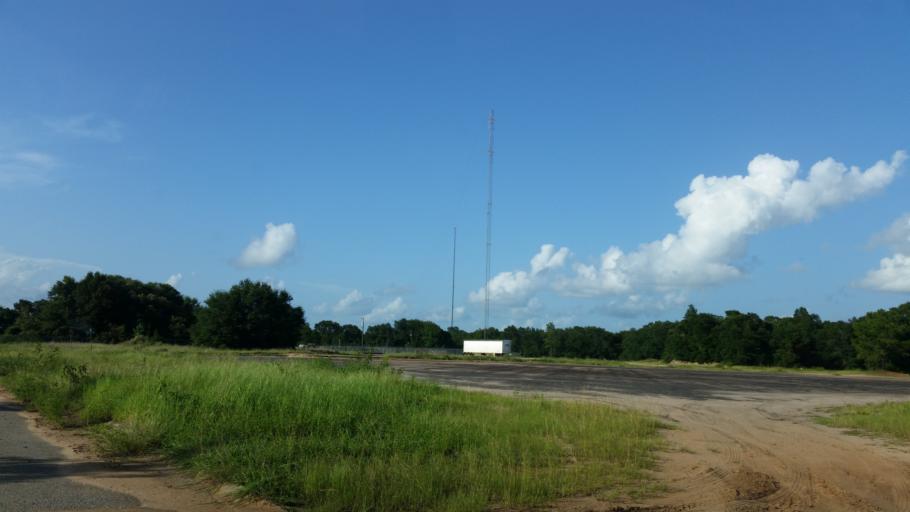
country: US
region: Florida
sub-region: Santa Rosa County
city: Bagdad
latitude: 30.5825
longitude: -87.0769
